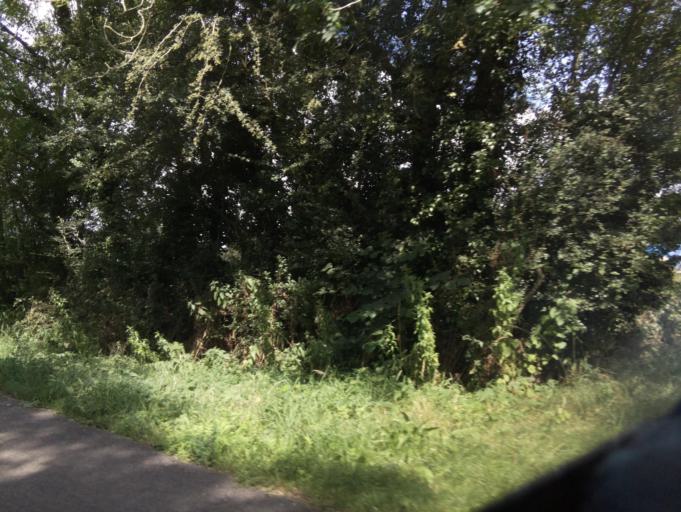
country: GB
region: England
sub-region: Wiltshire
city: Minety
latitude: 51.6177
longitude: -1.9947
